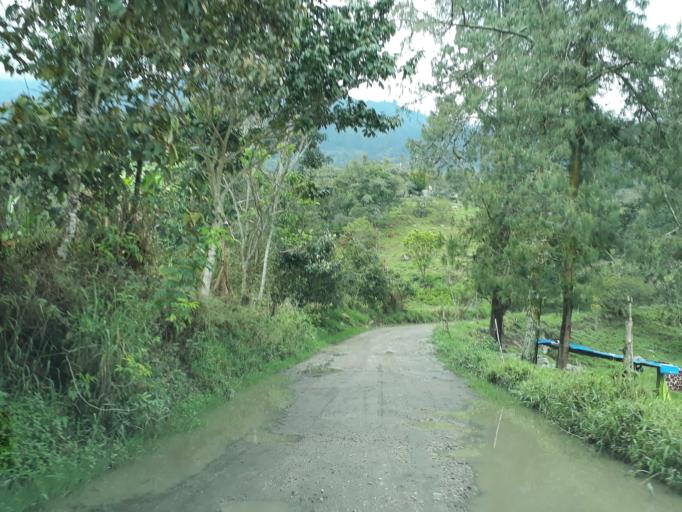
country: CO
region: Cundinamarca
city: Manta
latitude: 4.9878
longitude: -73.5585
